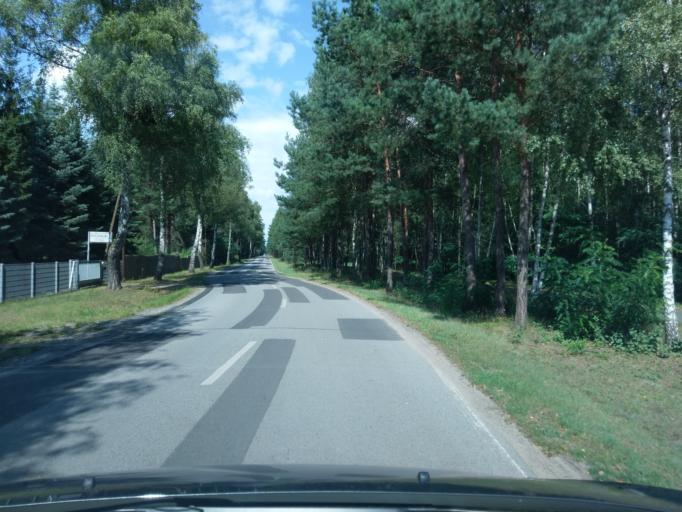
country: DE
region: Brandenburg
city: Borkwalde
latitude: 52.2542
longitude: 12.8352
